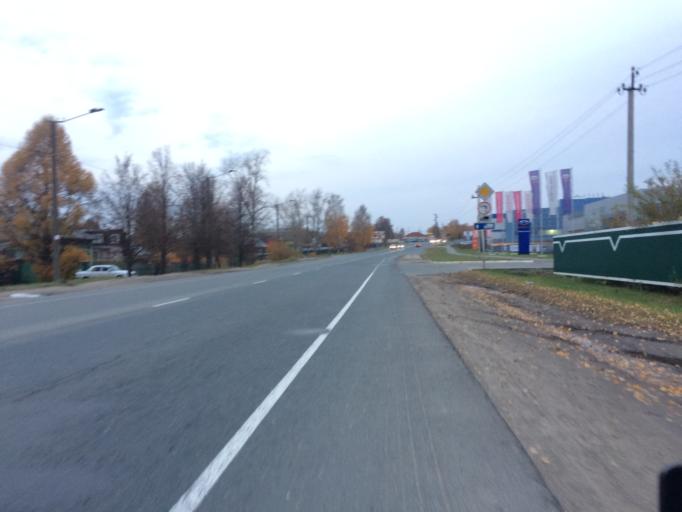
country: RU
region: Mariy-El
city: Yoshkar-Ola
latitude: 56.6034
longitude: 47.8822
